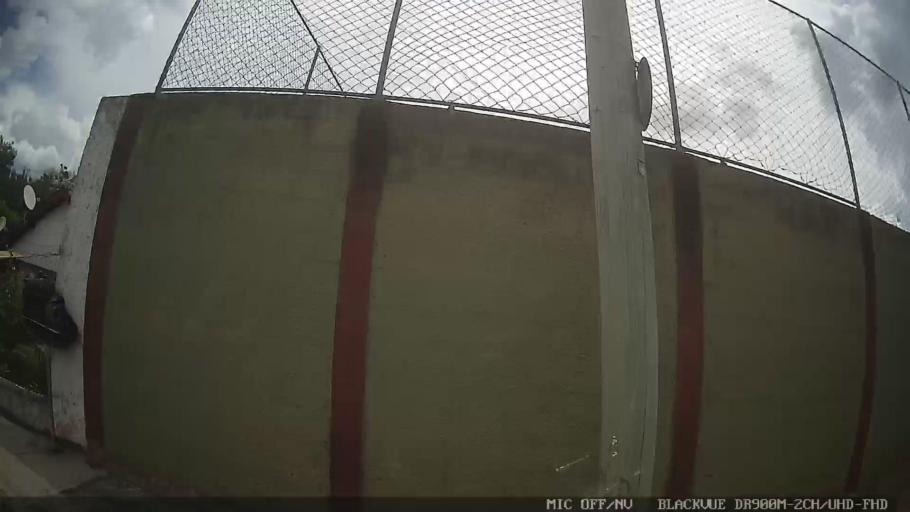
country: BR
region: Sao Paulo
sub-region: Atibaia
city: Atibaia
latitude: -23.1228
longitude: -46.5952
